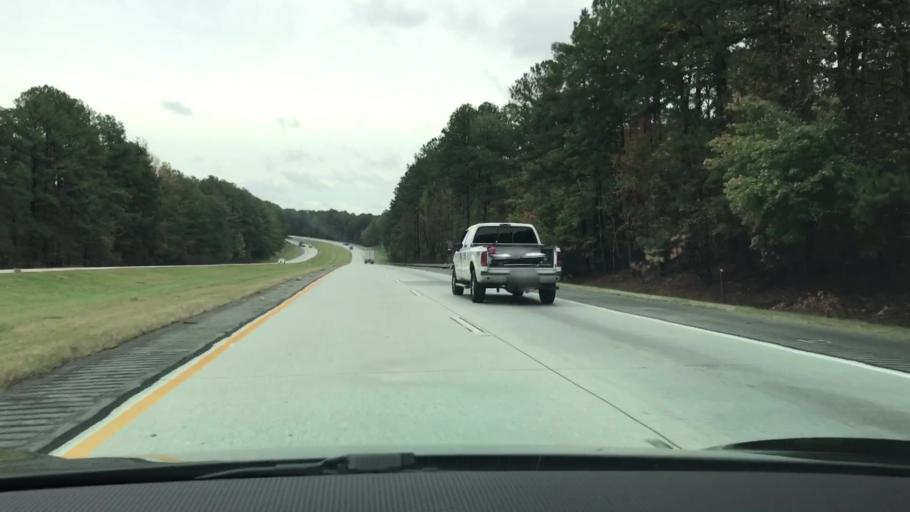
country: US
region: Georgia
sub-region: Taliaferro County
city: Crawfordville
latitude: 33.5007
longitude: -82.8218
